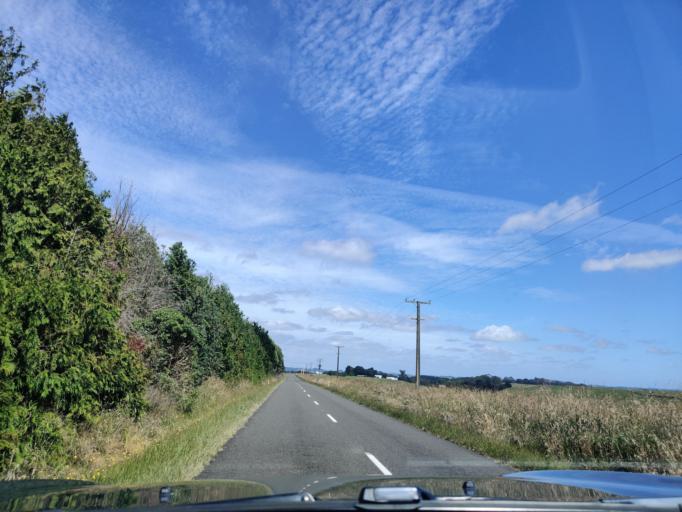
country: NZ
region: Manawatu-Wanganui
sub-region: Rangitikei District
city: Bulls
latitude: -40.1868
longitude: 175.4508
